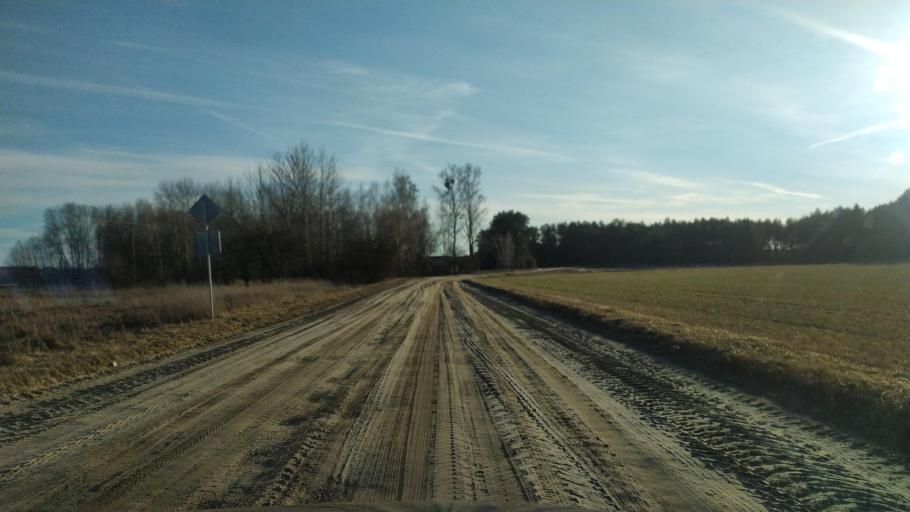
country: BY
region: Brest
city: Pruzhany
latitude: 52.5514
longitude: 24.2876
